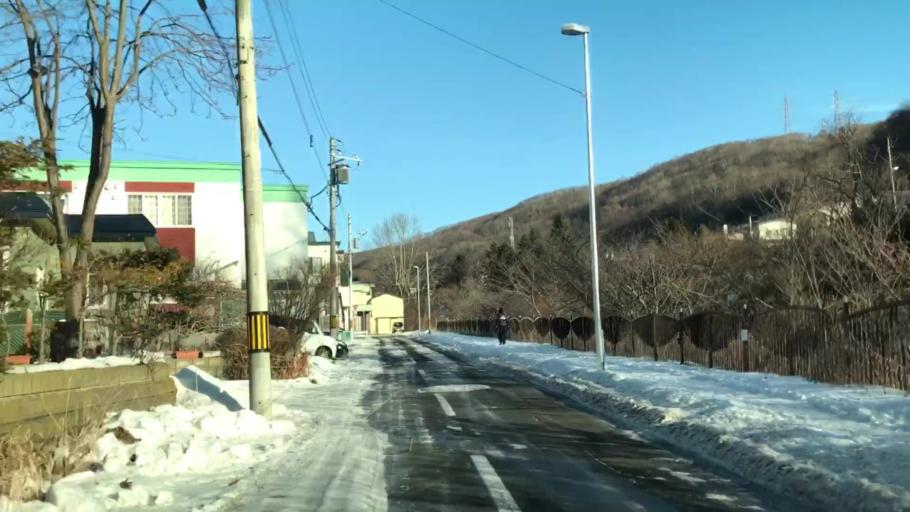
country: JP
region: Hokkaido
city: Muroran
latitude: 42.3757
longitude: 141.0374
